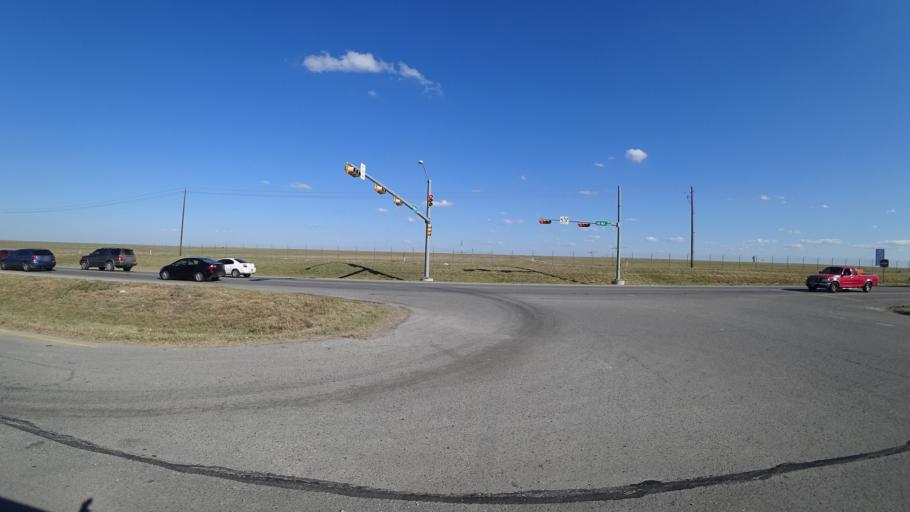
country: US
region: Texas
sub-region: Travis County
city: Austin
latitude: 30.2101
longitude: -97.6834
